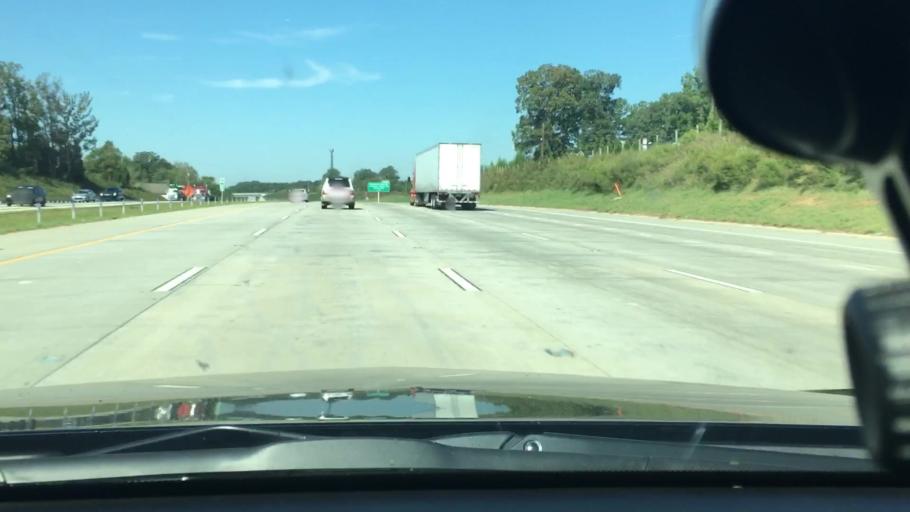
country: US
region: North Carolina
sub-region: Mecklenburg County
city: Huntersville
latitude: 35.3660
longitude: -80.7595
